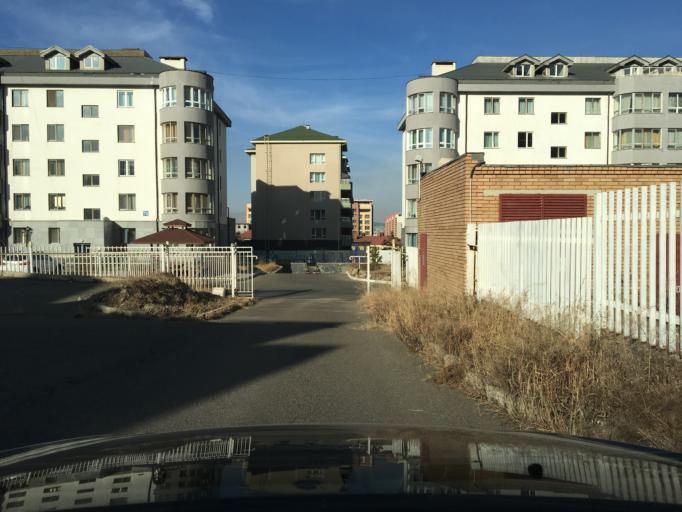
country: MN
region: Ulaanbaatar
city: Ulaanbaatar
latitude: 47.8786
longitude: 106.9104
